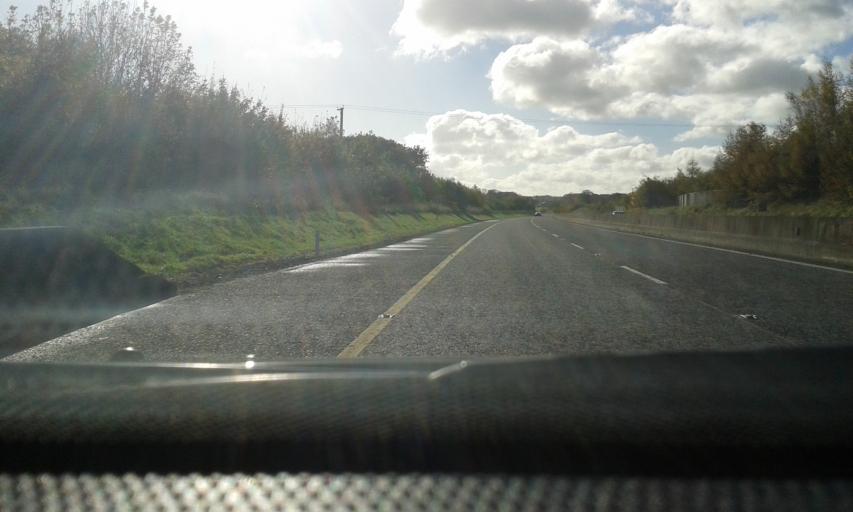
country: IE
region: Munster
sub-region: County Cork
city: Rathcormac
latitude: 52.0811
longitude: -8.2972
